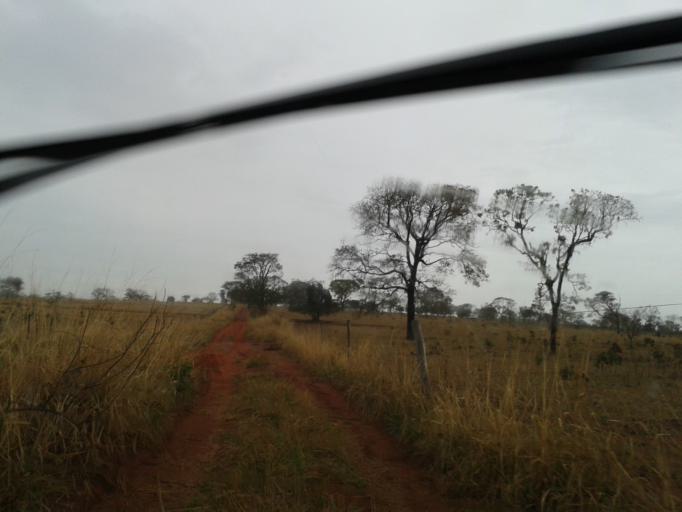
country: BR
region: Minas Gerais
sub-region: Campina Verde
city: Campina Verde
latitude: -19.3535
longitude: -49.5447
